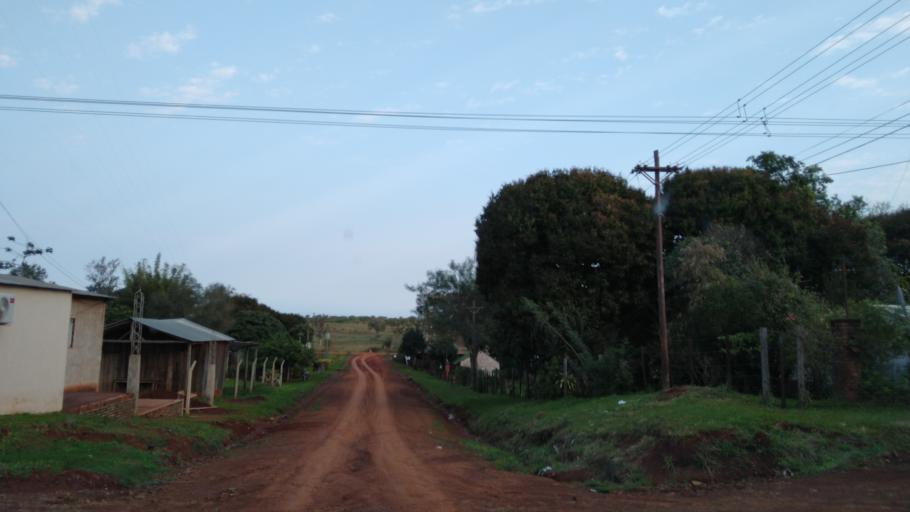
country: AR
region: Corrientes
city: San Carlos
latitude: -27.7506
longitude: -55.9007
